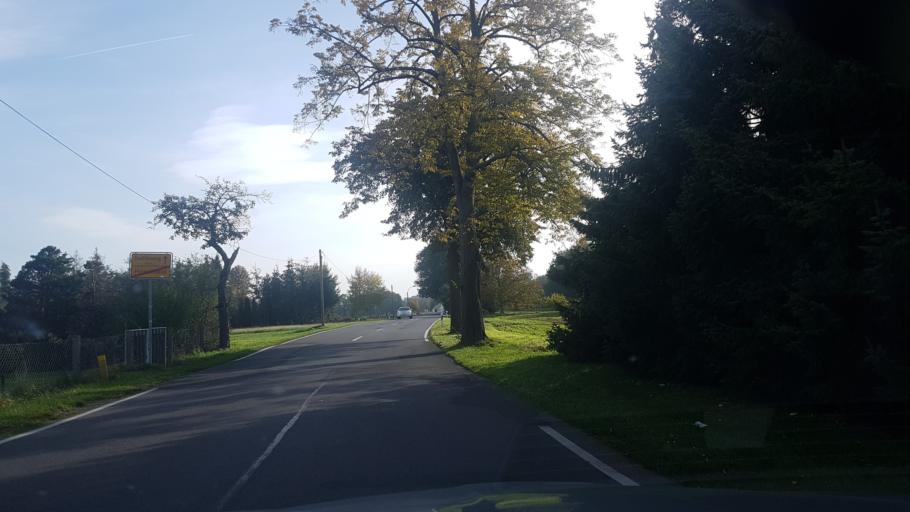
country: DE
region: Brandenburg
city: Hirschfeld
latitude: 51.3855
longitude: 13.6230
